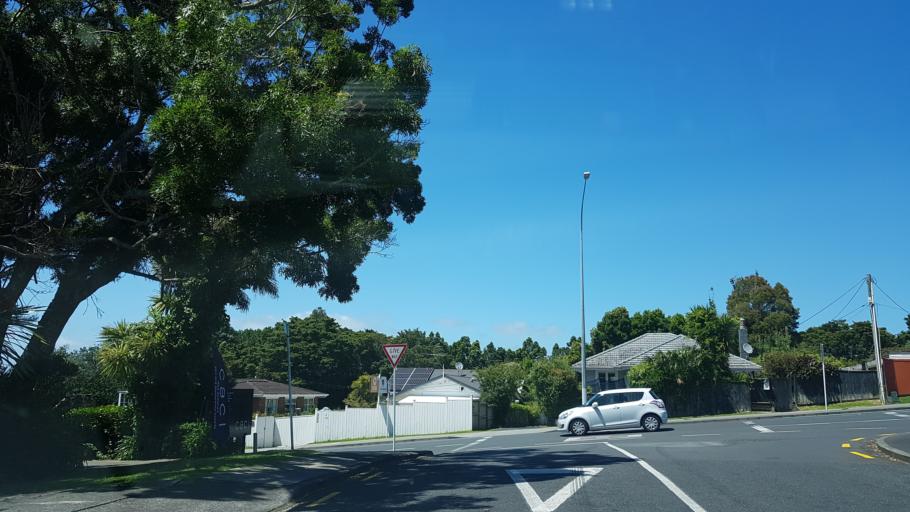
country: NZ
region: Auckland
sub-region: Auckland
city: North Shore
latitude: -36.8098
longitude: 174.7296
